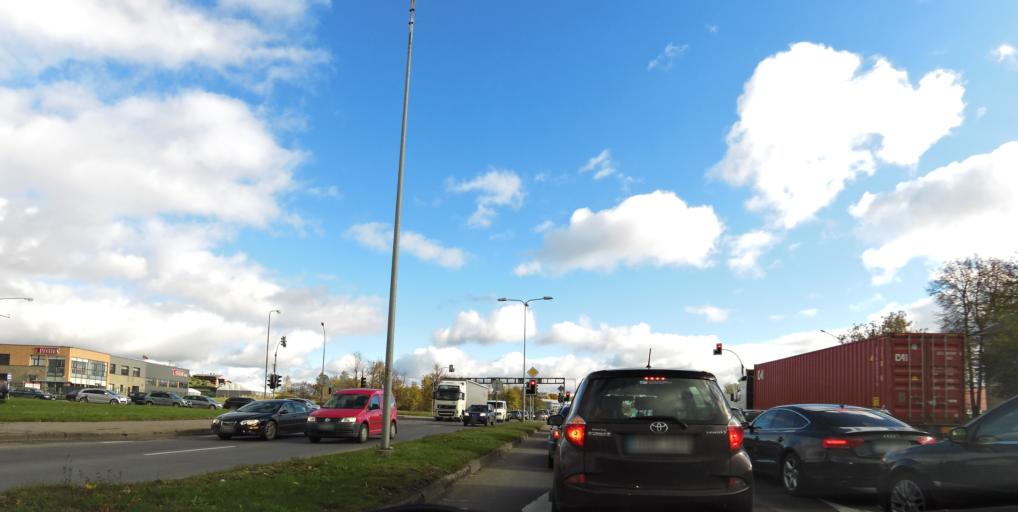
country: LT
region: Vilnius County
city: Rasos
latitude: 54.6544
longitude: 25.3020
